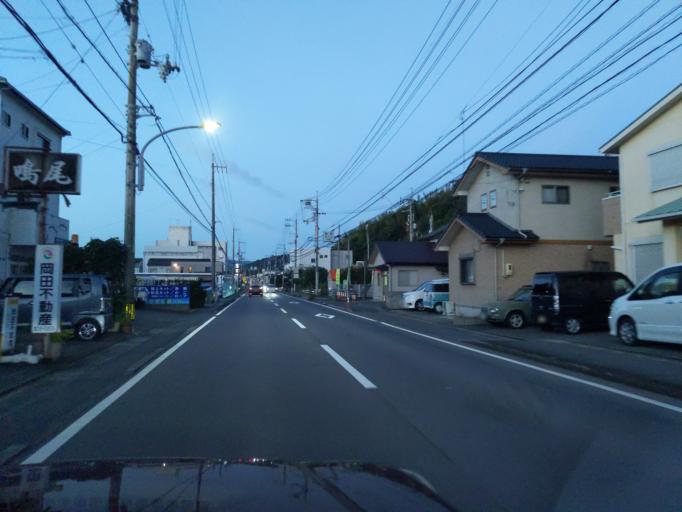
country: JP
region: Tokushima
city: Anan
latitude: 33.8779
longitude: 134.6490
